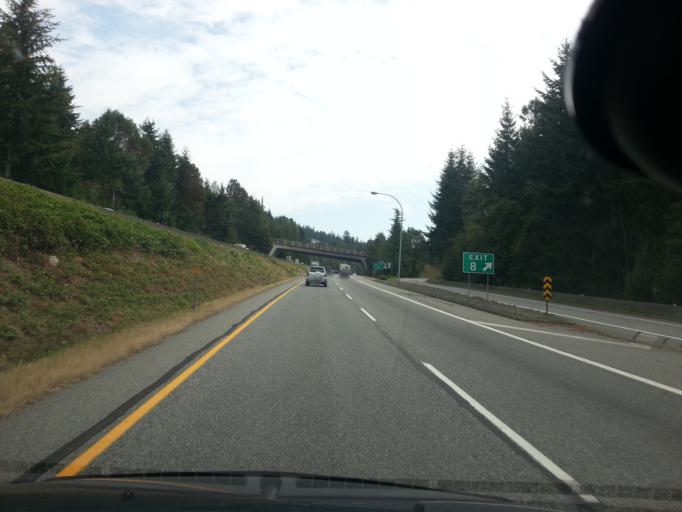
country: CA
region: British Columbia
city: West Vancouver
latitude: 49.3472
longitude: -123.1977
